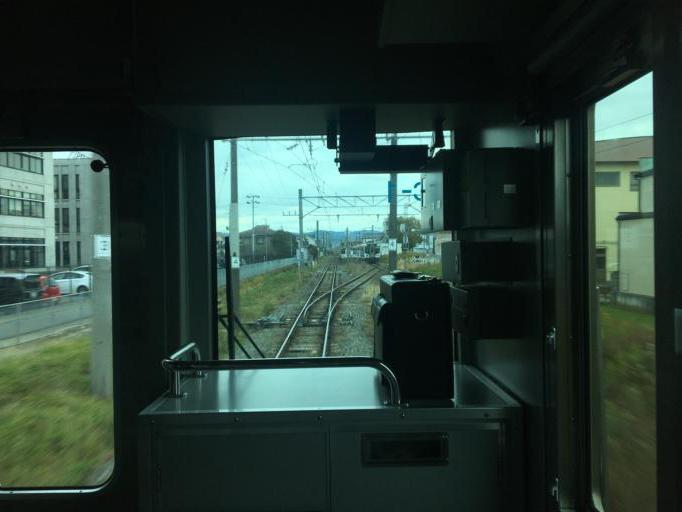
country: JP
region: Miyagi
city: Ishinomaki
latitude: 38.4371
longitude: 141.2865
